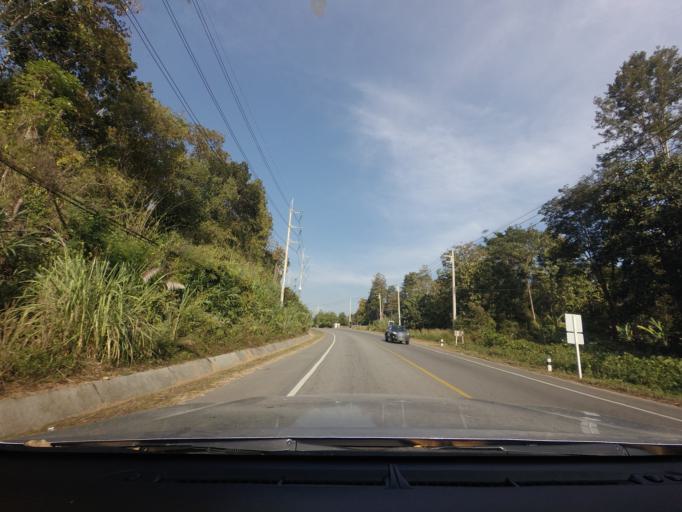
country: TH
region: Chiang Mai
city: Mae Taeng
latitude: 19.1027
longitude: 98.8199
